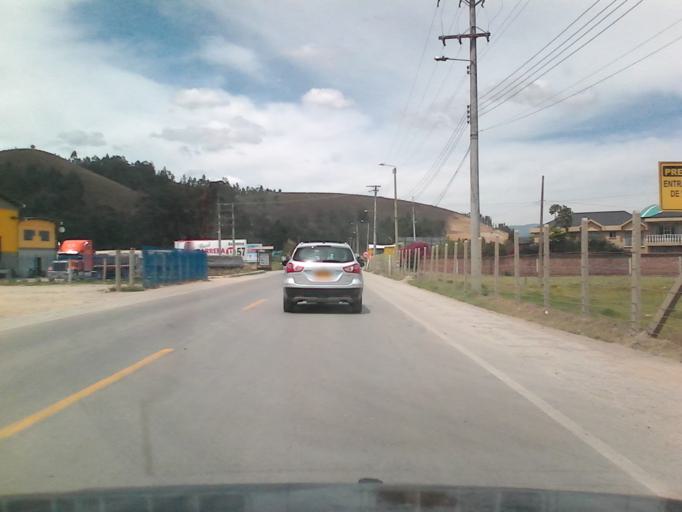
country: CO
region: Boyaca
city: Sogamoso
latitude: 5.7268
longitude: -72.9476
